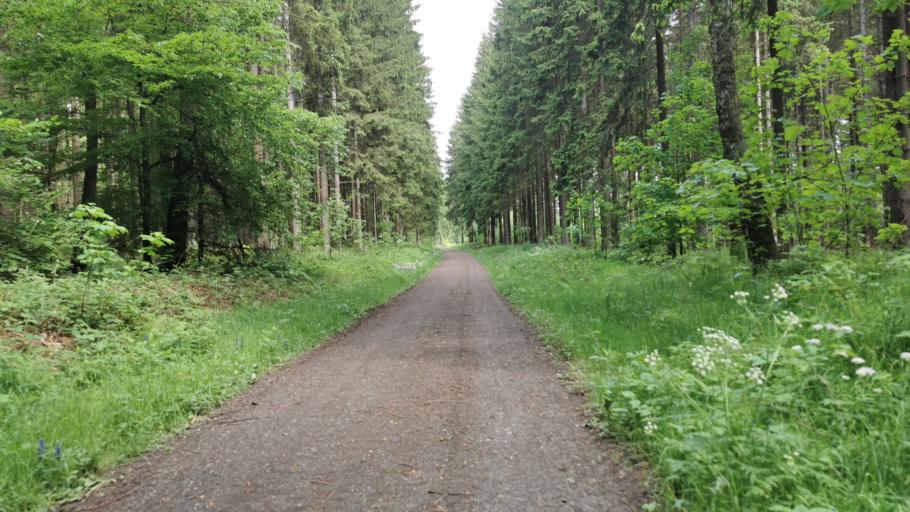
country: DE
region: Bavaria
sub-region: Upper Franconia
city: Ludwigsstadt
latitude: 50.4437
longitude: 11.3699
